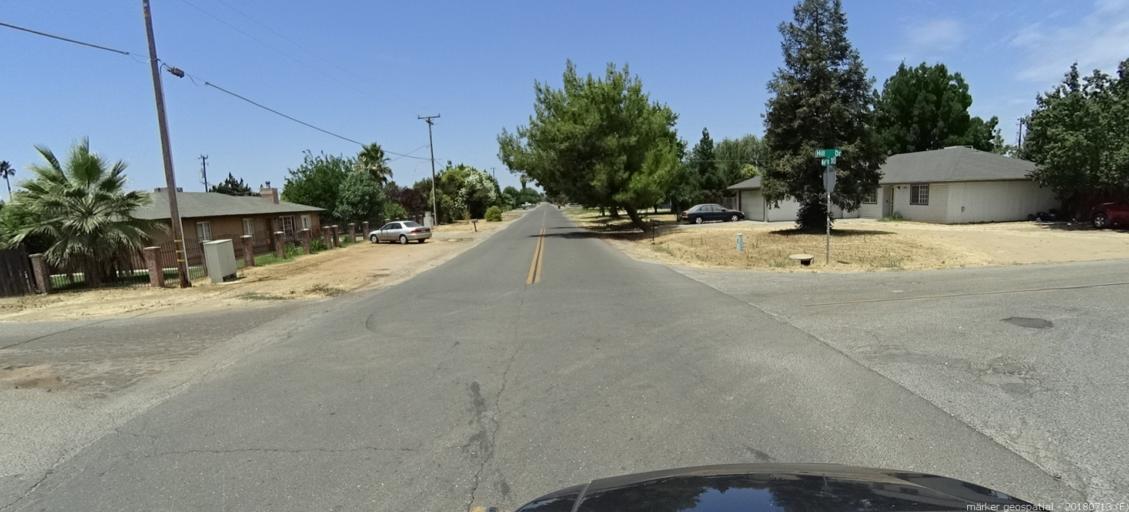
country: US
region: California
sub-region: Madera County
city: Madera Acres
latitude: 36.9928
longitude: -120.0753
